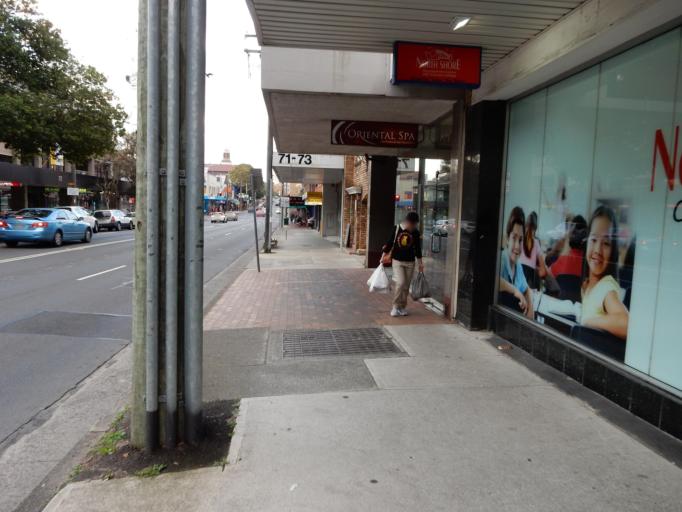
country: AU
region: New South Wales
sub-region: Willoughby
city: Chatswood
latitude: -33.7965
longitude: 151.1859
